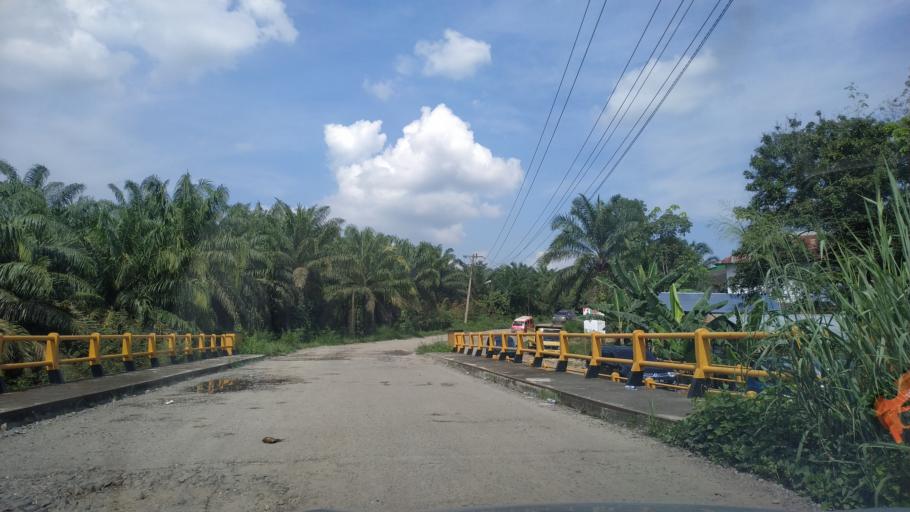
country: ID
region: North Sumatra
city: Binanga
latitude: 1.4144
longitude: 99.7470
